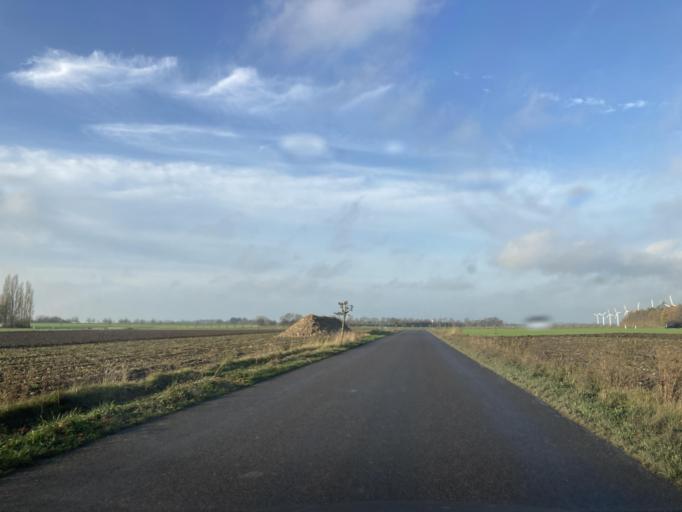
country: DK
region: Zealand
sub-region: Lolland Kommune
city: Rodby
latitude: 54.6899
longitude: 11.3729
